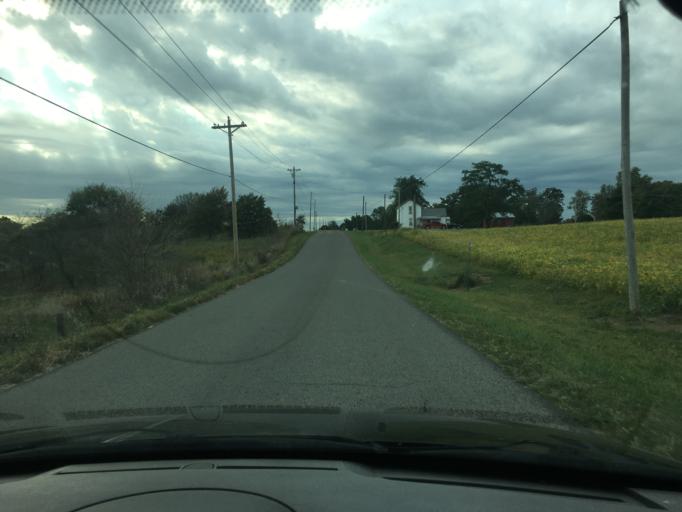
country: US
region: Ohio
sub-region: Logan County
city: Bellefontaine
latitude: 40.3339
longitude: -83.7931
